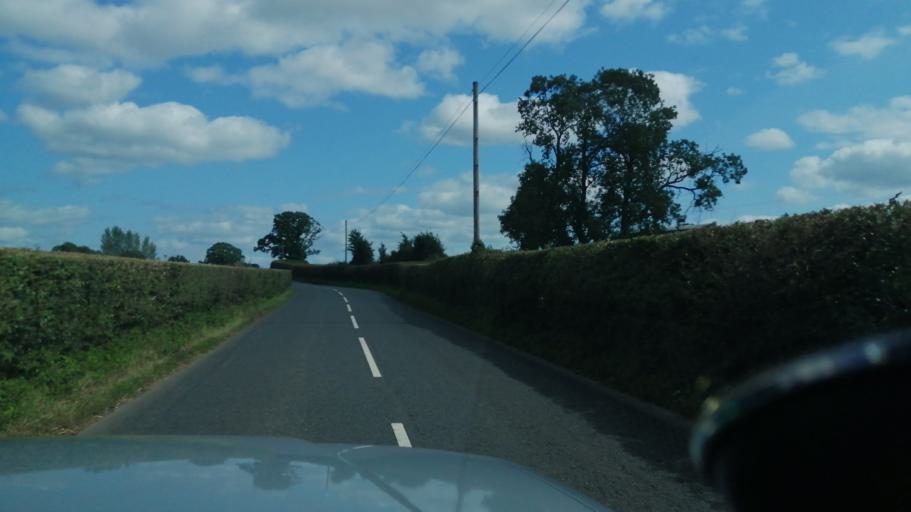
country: GB
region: England
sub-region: Herefordshire
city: Thruxton
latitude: 52.0088
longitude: -2.8243
